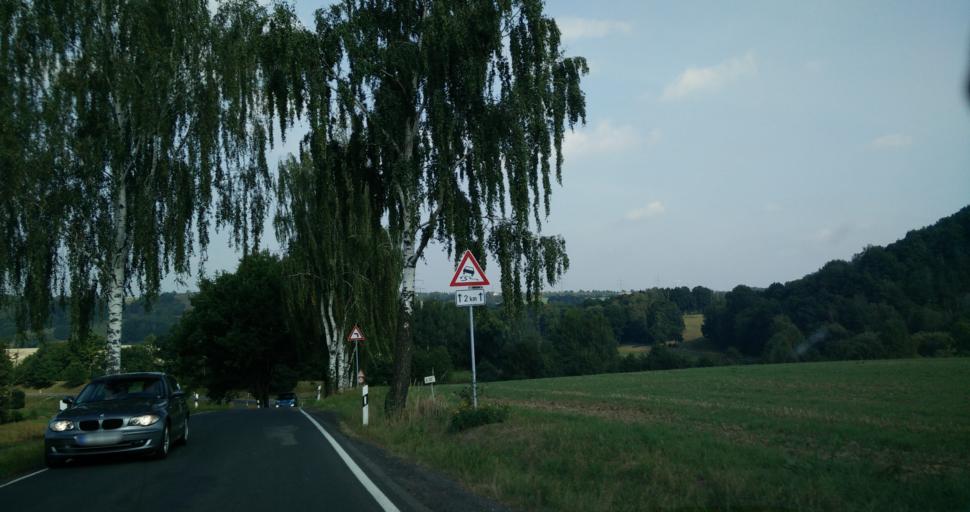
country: DE
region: Saxony
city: Colditz
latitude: 51.1057
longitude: 12.8052
